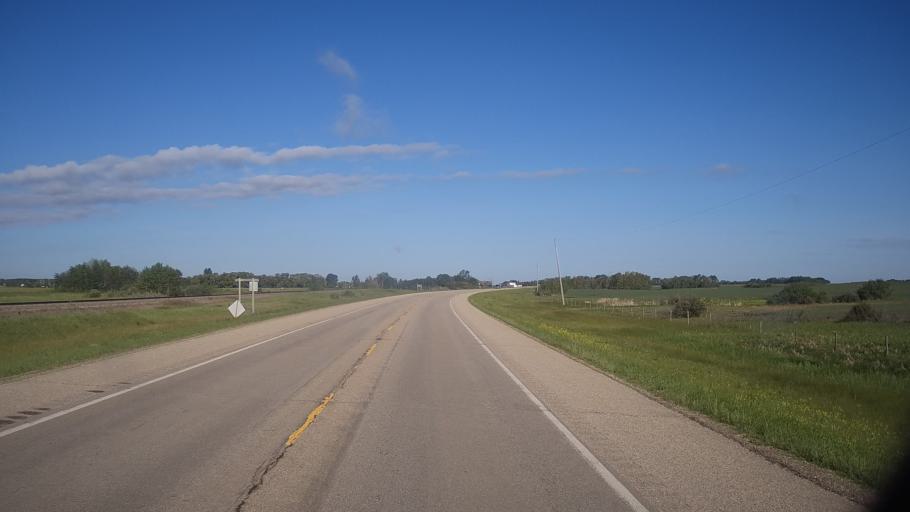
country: CA
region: Saskatchewan
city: Lanigan
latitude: 51.8711
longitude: -105.1719
